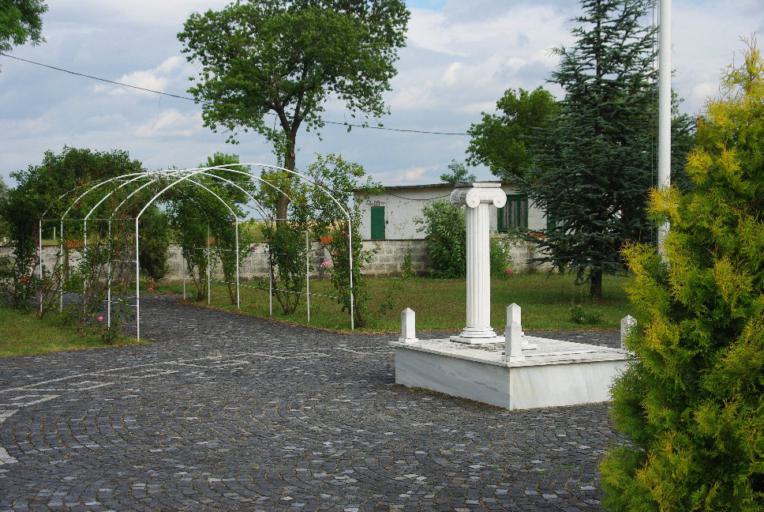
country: HU
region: Fejer
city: Ivancsa
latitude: 47.1800
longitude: 18.8234
